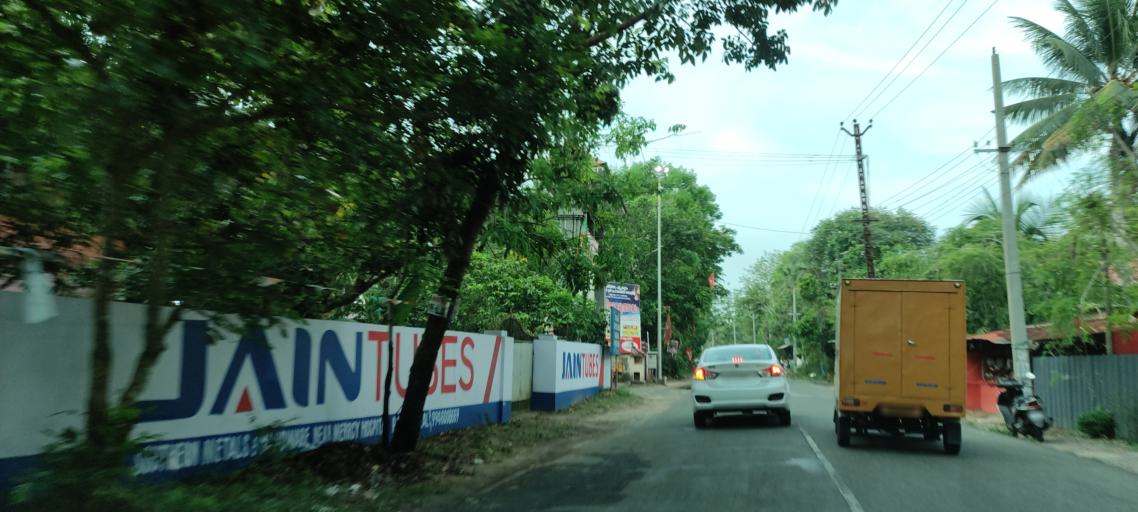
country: IN
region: Kerala
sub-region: Kottayam
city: Vaikam
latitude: 9.7609
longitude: 76.3626
